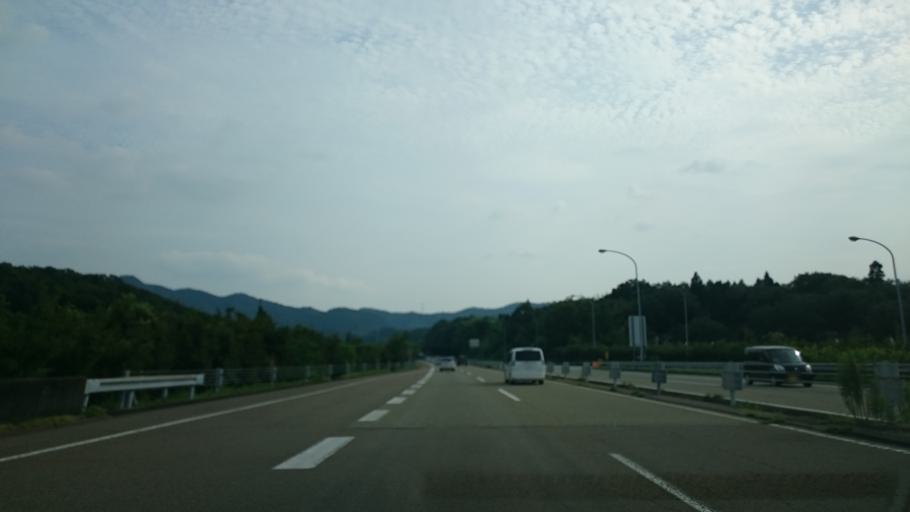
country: JP
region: Gifu
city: Kakamigahara
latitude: 35.4667
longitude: 136.8918
